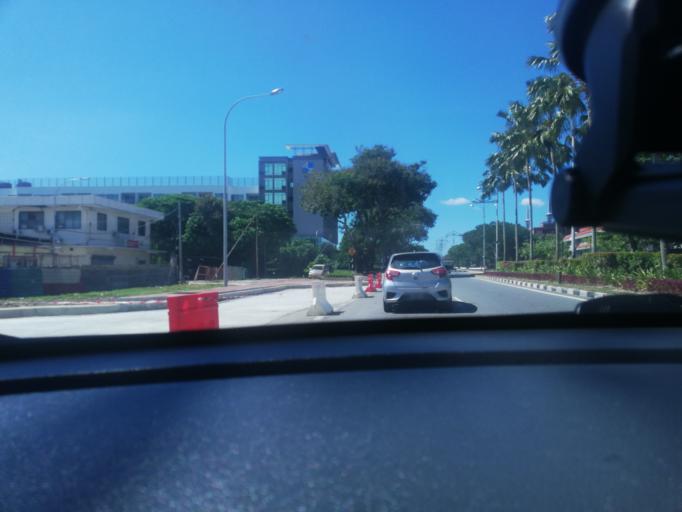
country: MY
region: Labuan
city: Victoria
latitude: 5.2797
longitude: 115.2446
